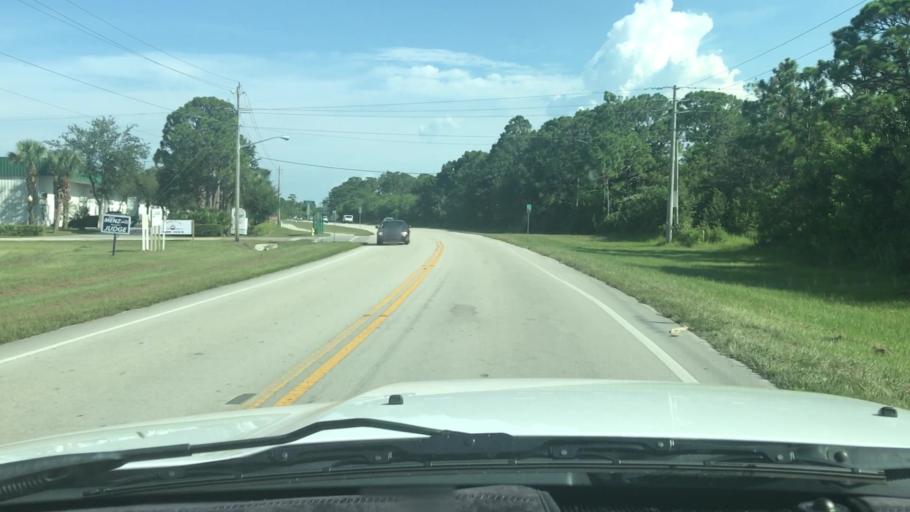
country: US
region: Florida
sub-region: Indian River County
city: Gifford
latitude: 27.6560
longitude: -80.4321
